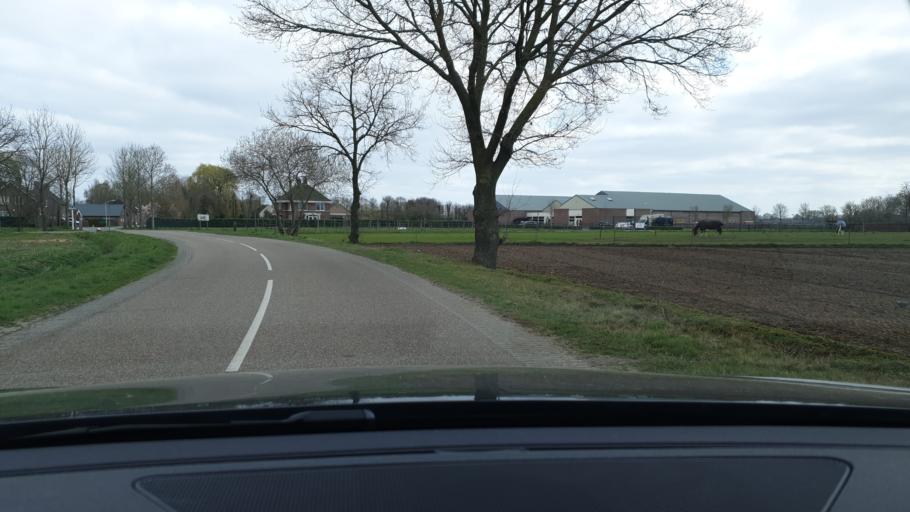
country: NL
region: North Brabant
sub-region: Gemeente Best
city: Best
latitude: 51.5232
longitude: 5.3523
